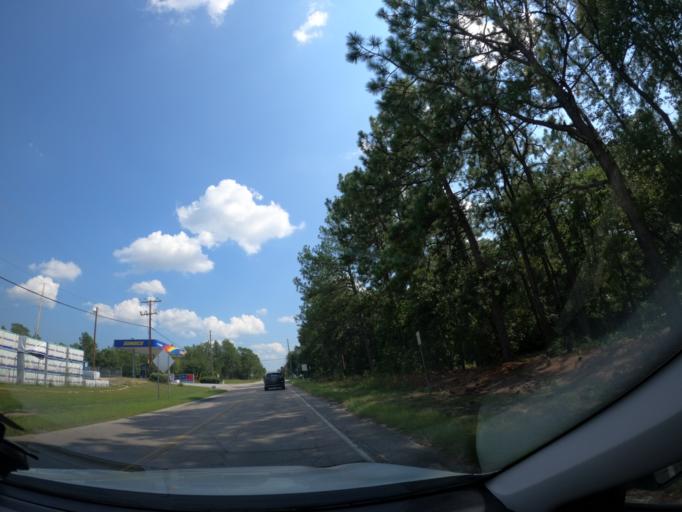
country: US
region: South Carolina
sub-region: Lexington County
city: Oak Grove
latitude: 33.9751
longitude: -81.1272
